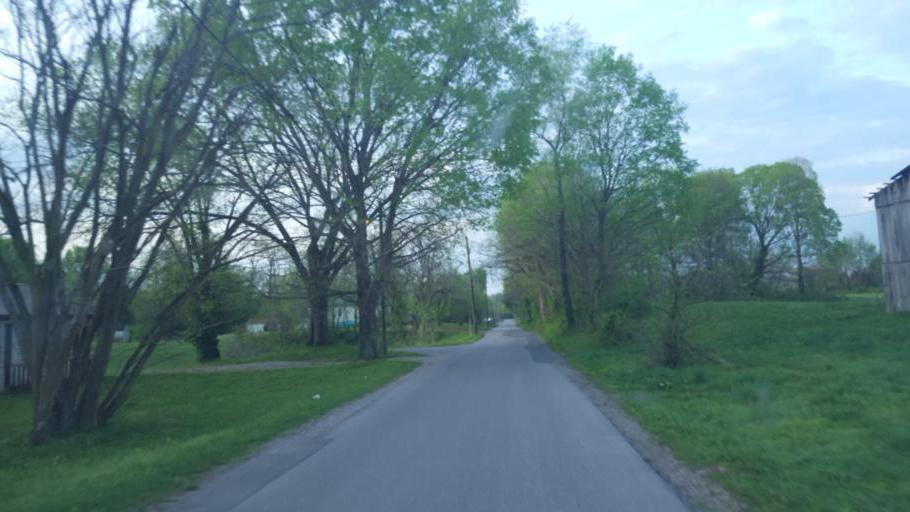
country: US
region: Kentucky
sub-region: Hart County
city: Munfordville
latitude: 37.2804
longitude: -85.9032
